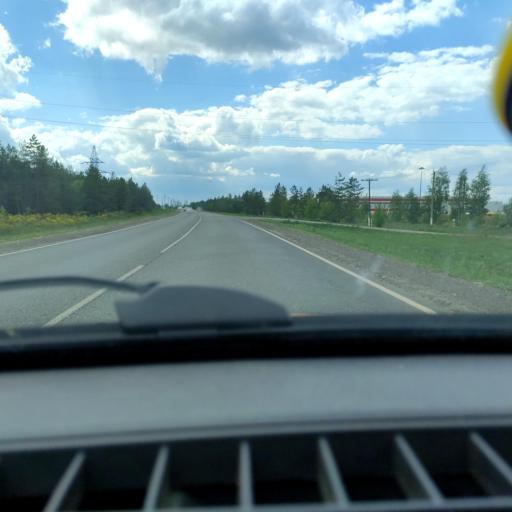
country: RU
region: Samara
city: Zhigulevsk
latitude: 53.5726
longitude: 49.5536
